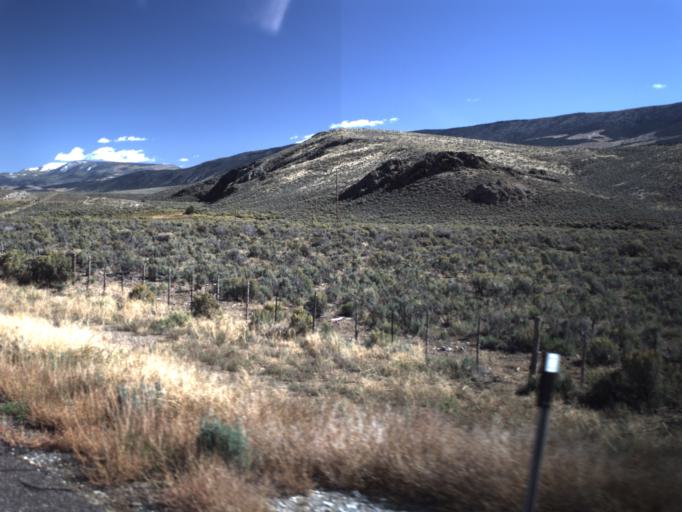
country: US
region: Utah
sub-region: Piute County
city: Junction
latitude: 38.3473
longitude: -111.9518
